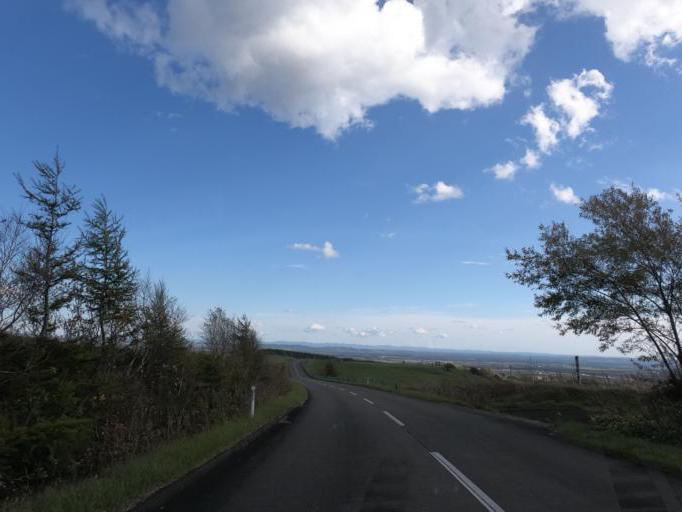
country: JP
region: Hokkaido
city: Otofuke
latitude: 43.2797
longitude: 143.2226
